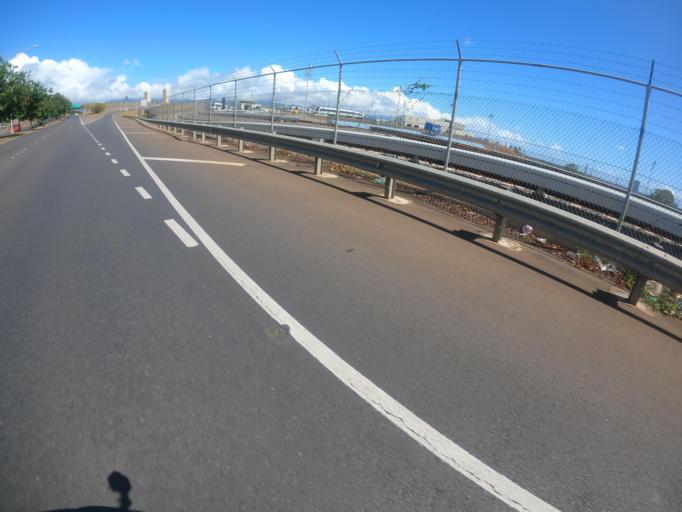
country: US
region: Hawaii
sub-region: Honolulu County
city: Pearl City, Manana
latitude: 21.3920
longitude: -157.9916
